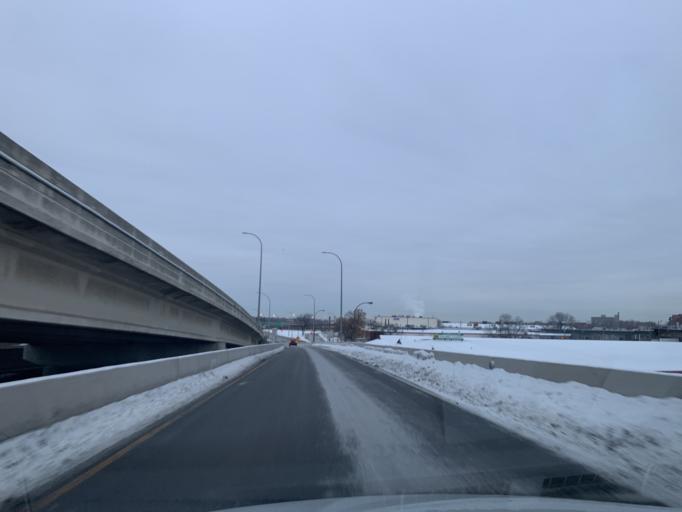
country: US
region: Minnesota
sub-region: Hennepin County
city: Minneapolis
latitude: 44.9803
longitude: -93.2869
